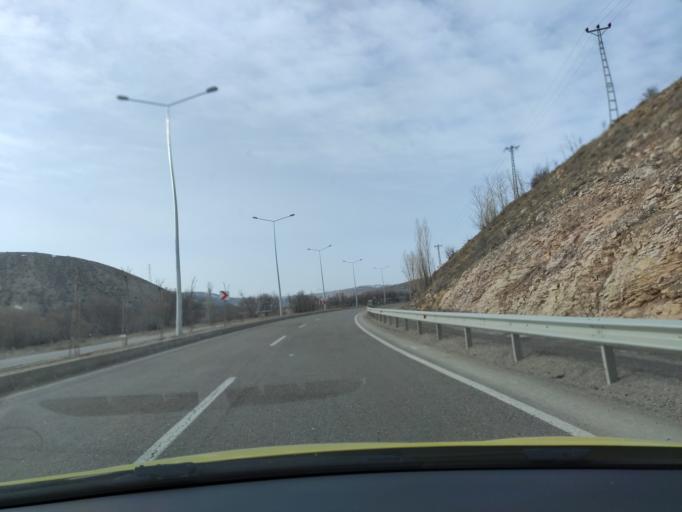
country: TR
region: Bayburt
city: Bayburt
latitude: 40.2274
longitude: 40.2591
